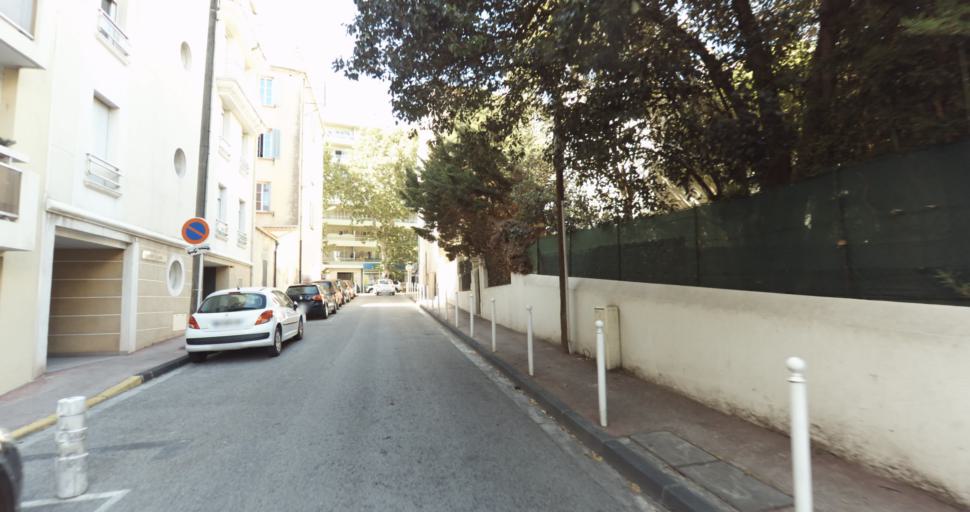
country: FR
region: Provence-Alpes-Cote d'Azur
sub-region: Departement du Var
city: Toulon
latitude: 43.1218
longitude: 5.9441
